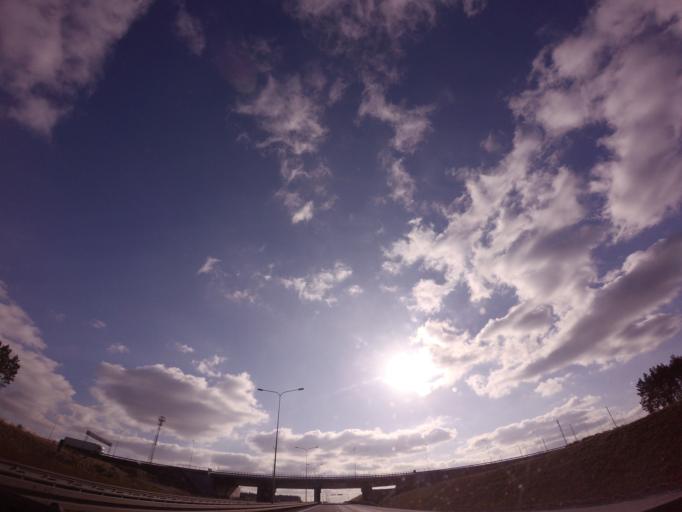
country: PL
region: Lubusz
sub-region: Powiat swiebodzinski
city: Swiebodzin
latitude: 52.3243
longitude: 15.5524
